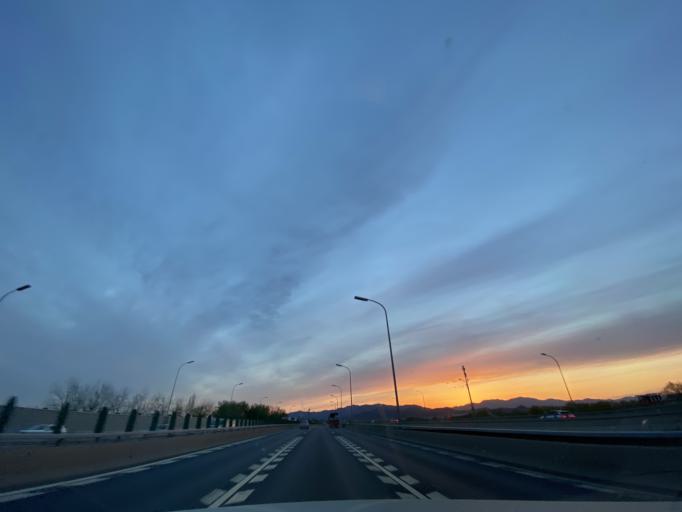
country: CN
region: Beijing
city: Qinghe
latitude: 40.0185
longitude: 116.3180
